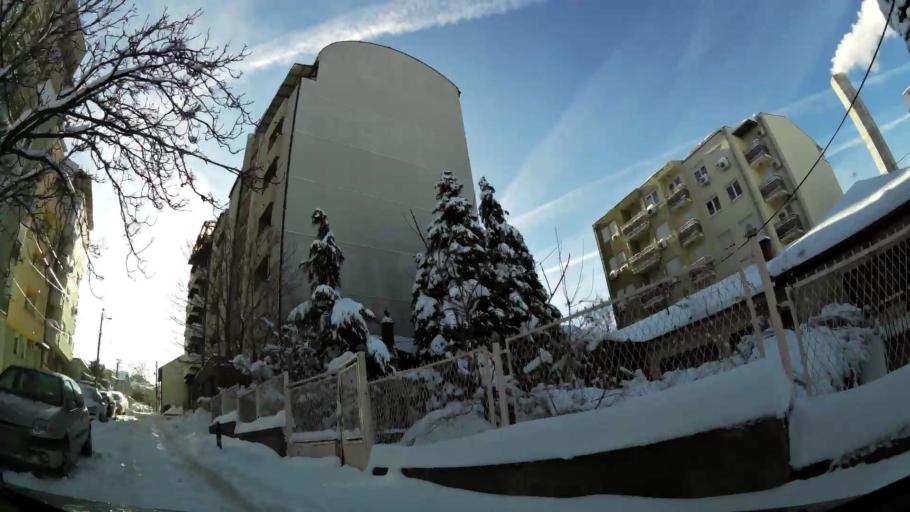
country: RS
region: Central Serbia
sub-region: Belgrade
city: Zvezdara
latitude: 44.7865
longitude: 20.5155
